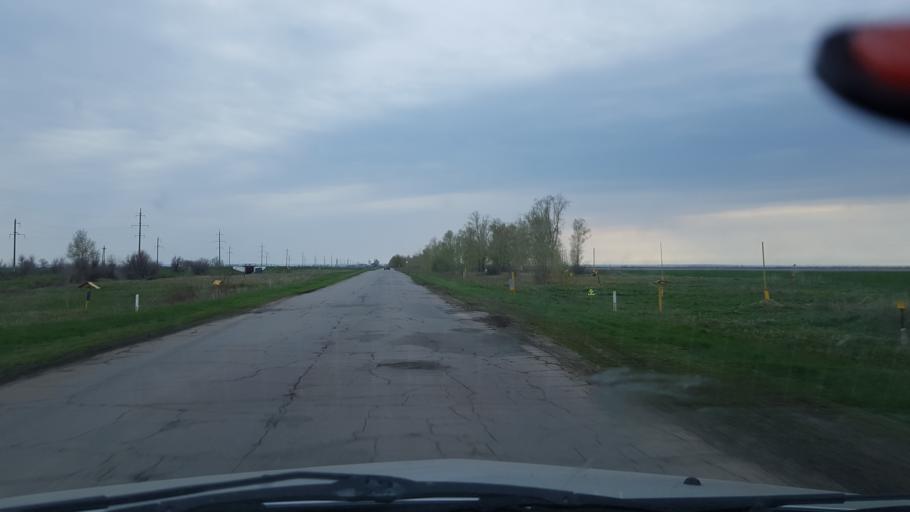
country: RU
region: Samara
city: Khryashchevka
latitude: 53.6691
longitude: 49.1292
